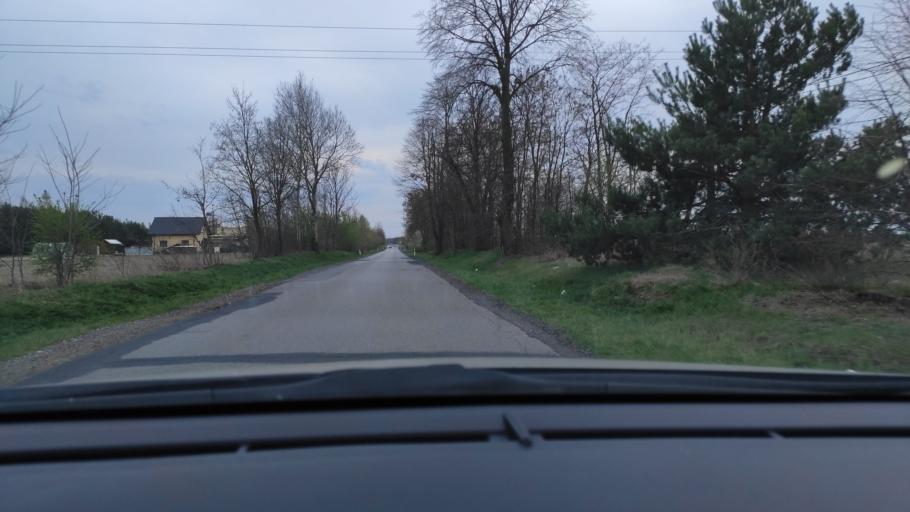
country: PL
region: Masovian Voivodeship
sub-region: Powiat zwolenski
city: Zwolen
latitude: 51.3678
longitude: 21.5640
